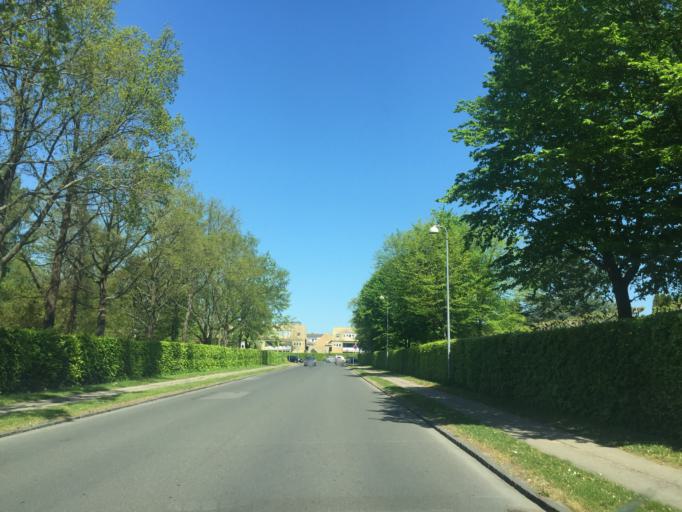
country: DK
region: South Denmark
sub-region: Odense Kommune
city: Odense
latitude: 55.3894
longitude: 10.3686
